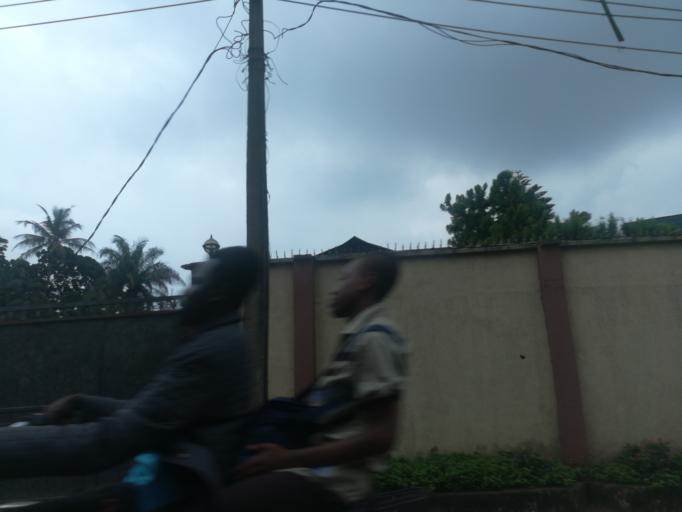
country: NG
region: Lagos
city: Ojota
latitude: 6.5686
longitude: 3.3693
